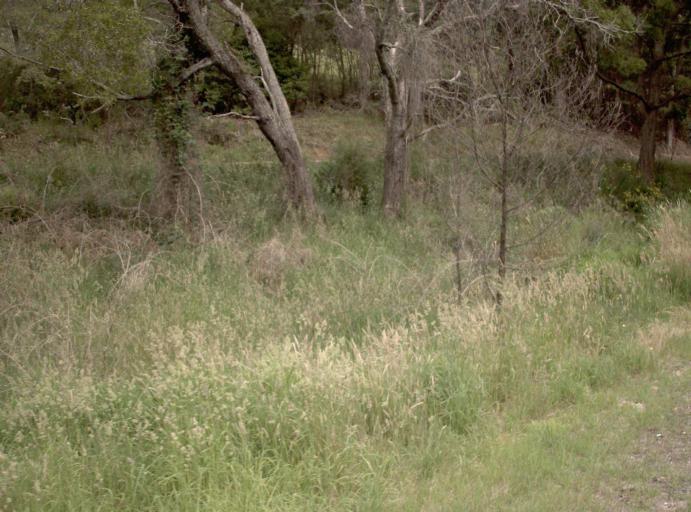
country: AU
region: New South Wales
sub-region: Bombala
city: Bombala
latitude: -37.4317
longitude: 149.1980
